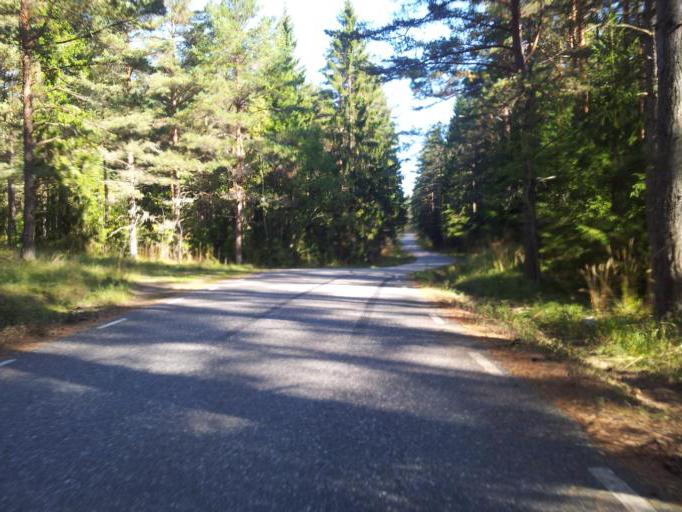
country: SE
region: Stockholm
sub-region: Norrtalje Kommun
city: Nykvarn
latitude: 59.8643
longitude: 18.2216
